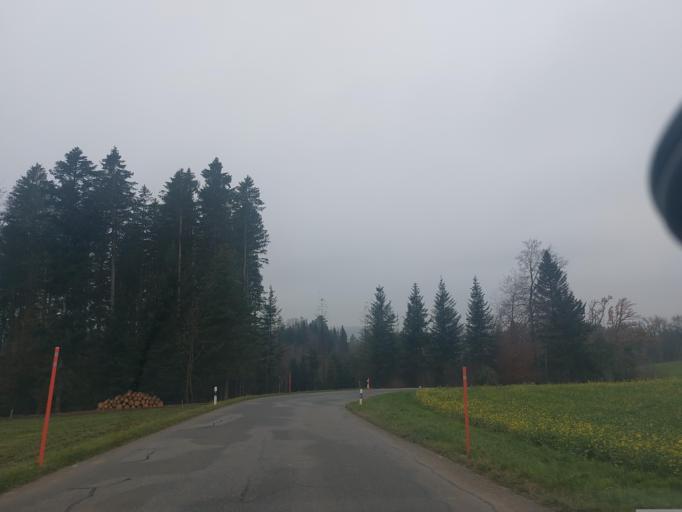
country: CH
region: Vaud
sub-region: Lavaux-Oron District
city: Palezieux
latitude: 46.5449
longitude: 6.8486
